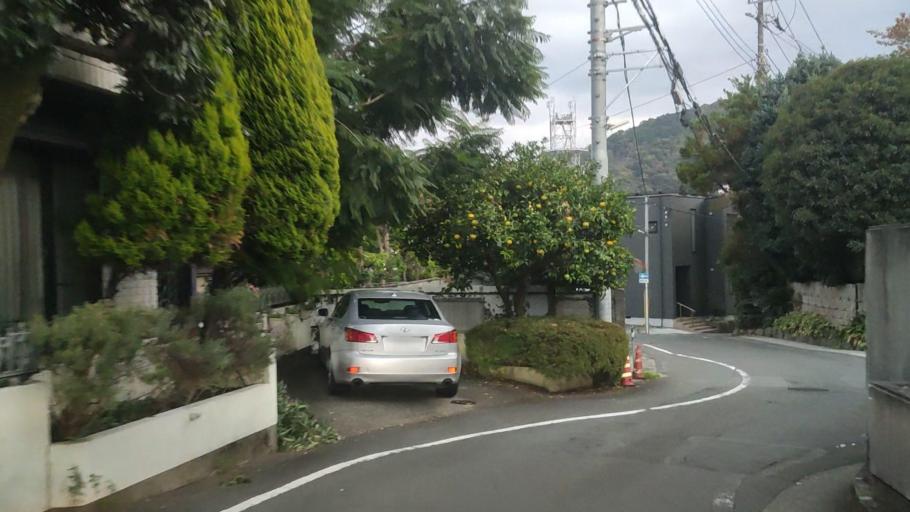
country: JP
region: Shizuoka
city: Atami
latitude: 35.0962
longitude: 139.0672
